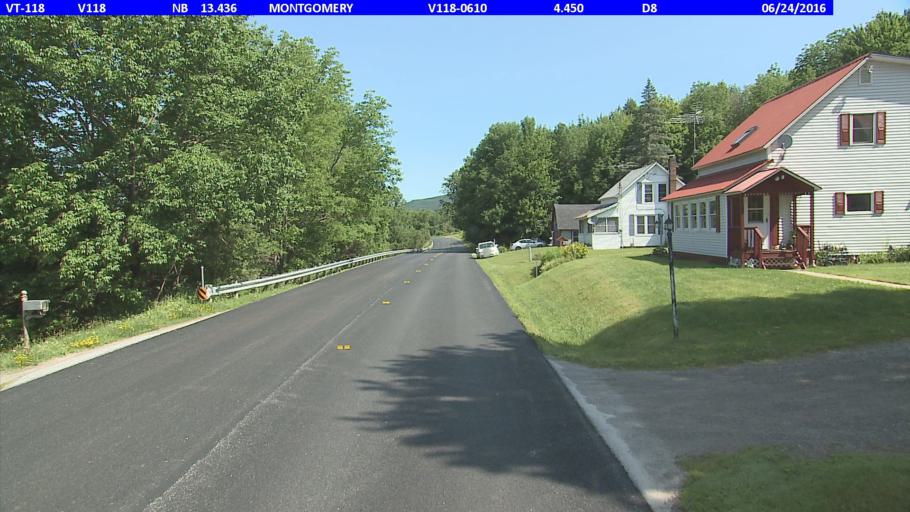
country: US
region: Vermont
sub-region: Franklin County
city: Richford
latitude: 44.8617
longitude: -72.6096
